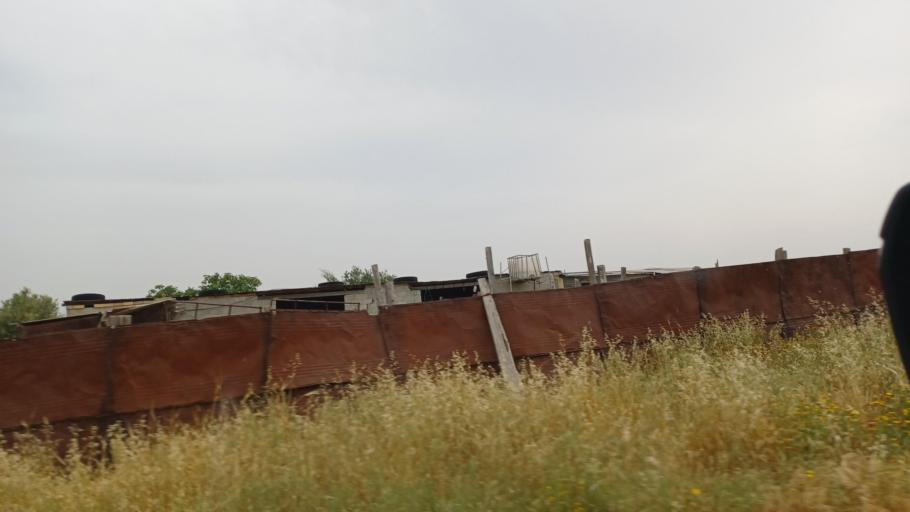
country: CY
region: Lefkosia
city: Mammari
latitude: 35.1778
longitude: 33.1967
